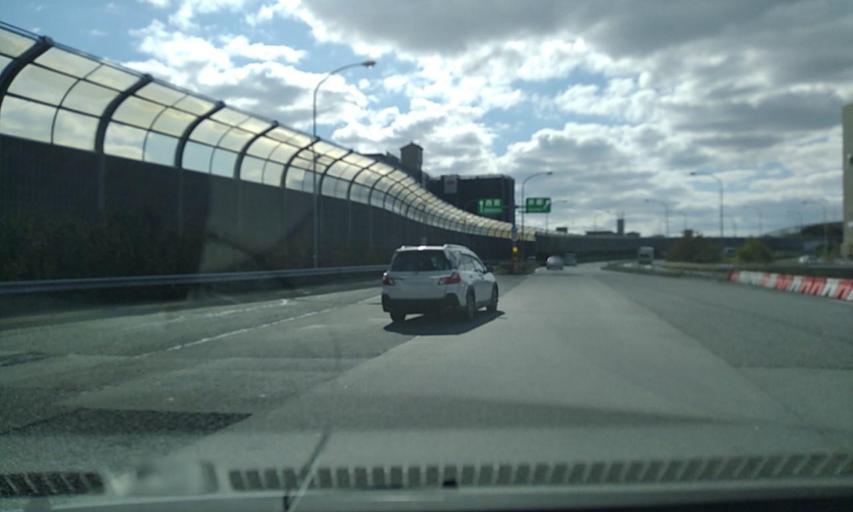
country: JP
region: Osaka
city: Ibaraki
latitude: 34.8046
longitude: 135.5446
